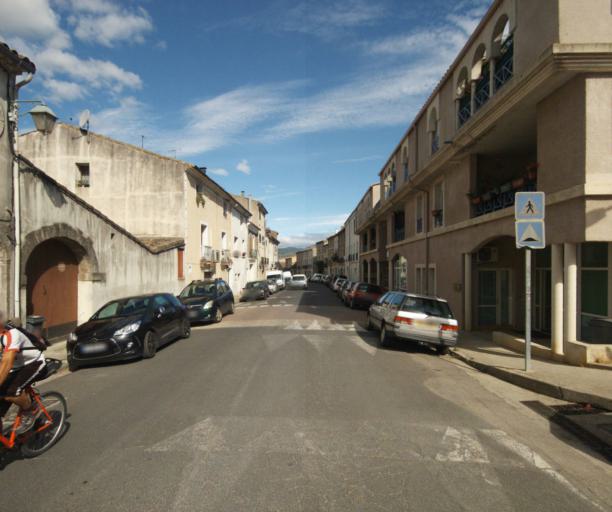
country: FR
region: Languedoc-Roussillon
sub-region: Departement de l'Herault
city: Aniane
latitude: 43.6847
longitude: 3.5897
